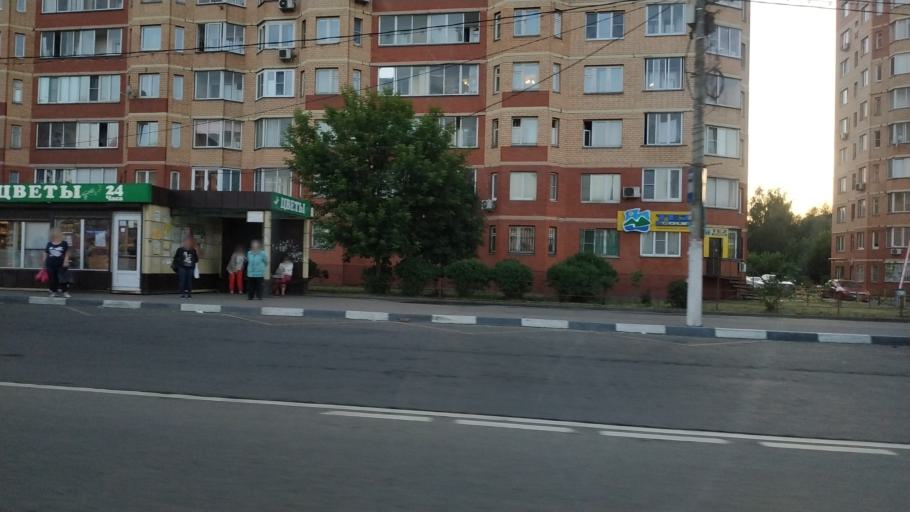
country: RU
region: Moskovskaya
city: Shchelkovo
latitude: 55.9205
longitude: 37.9978
